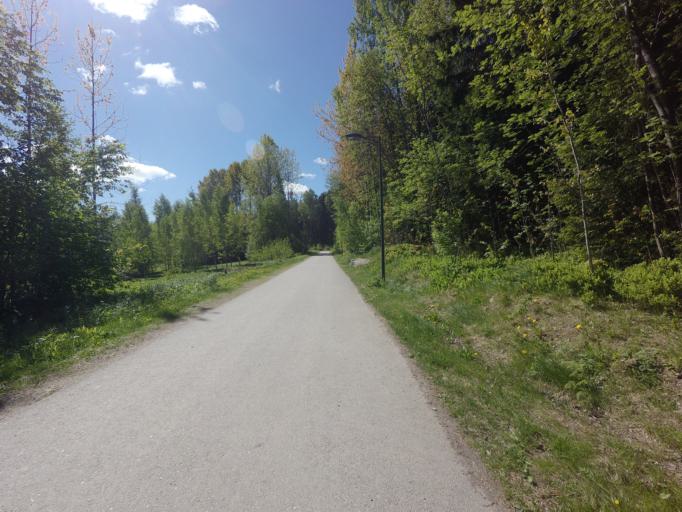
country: FI
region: Uusimaa
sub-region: Helsinki
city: Kauniainen
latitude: 60.1839
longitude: 24.7378
